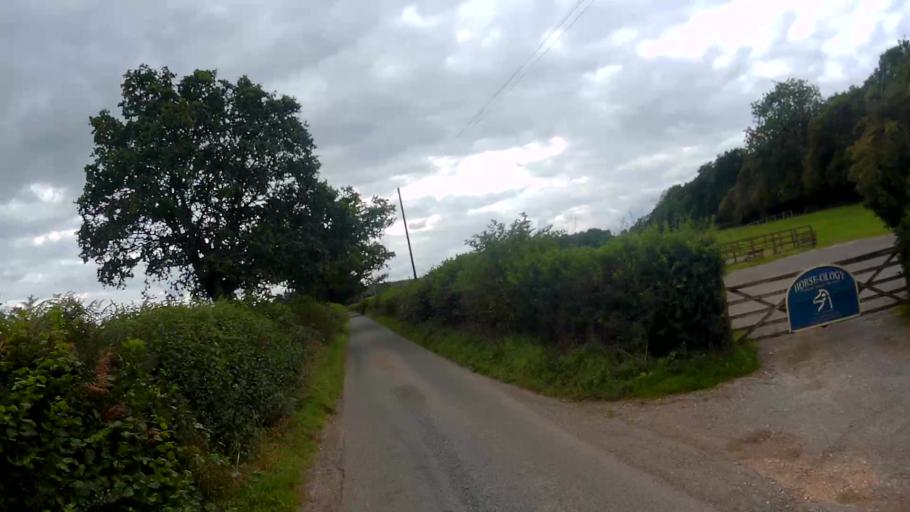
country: GB
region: England
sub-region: Hampshire
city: Overton
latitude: 51.2108
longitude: -1.2316
